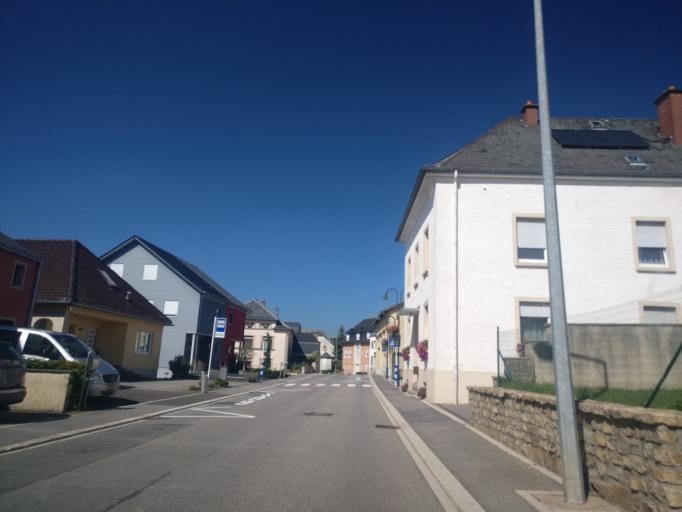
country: DE
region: Rheinland-Pfalz
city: Wellen
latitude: 49.6494
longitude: 6.3997
